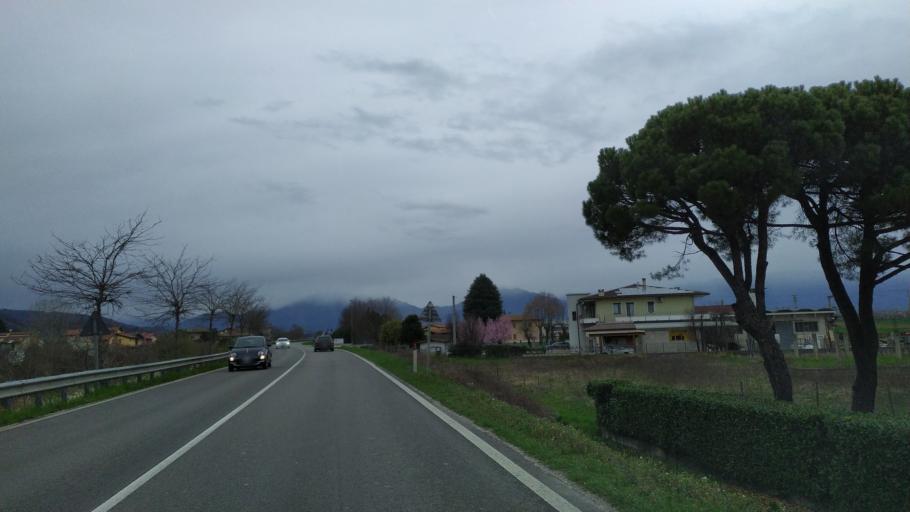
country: IT
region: Veneto
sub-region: Provincia di Vicenza
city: Castelnovo
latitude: 45.6111
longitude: 11.4700
